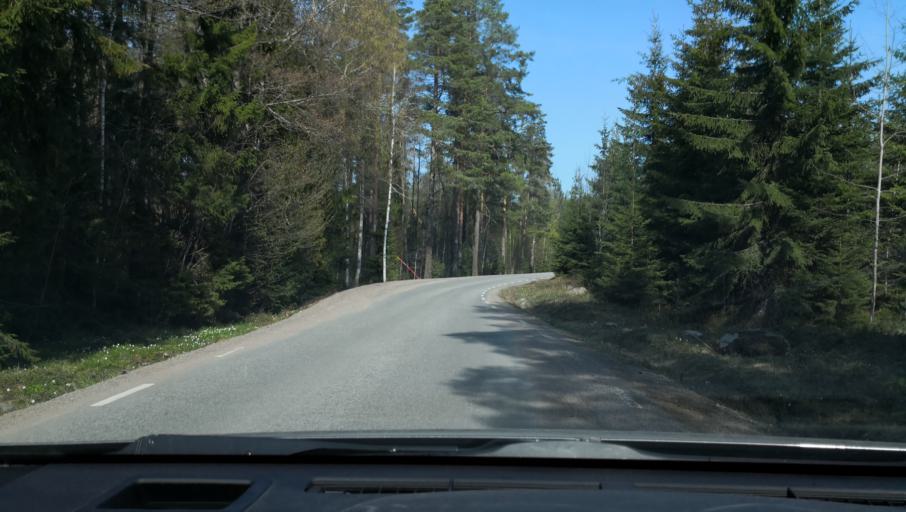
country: SE
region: Vaestmanland
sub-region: Sala Kommun
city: Sala
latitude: 60.0011
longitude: 16.6649
